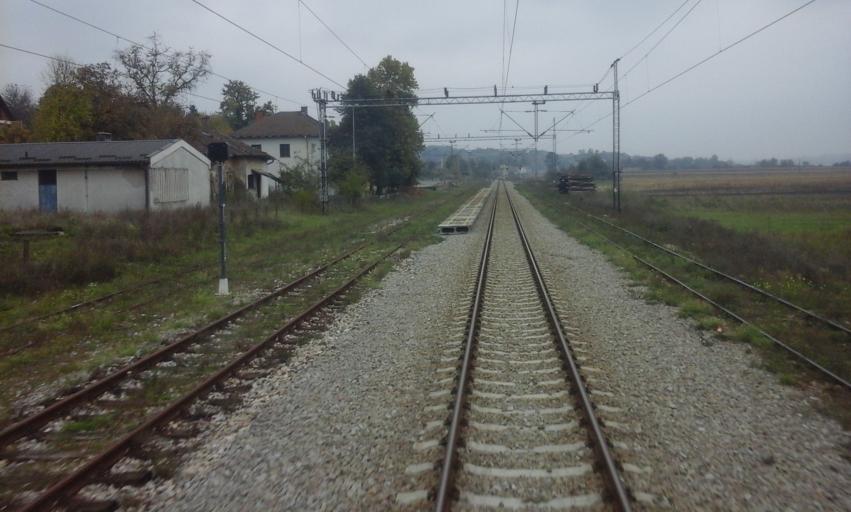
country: RS
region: Central Serbia
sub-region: Belgrade
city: Mladenovac
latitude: 44.4815
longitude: 20.6596
